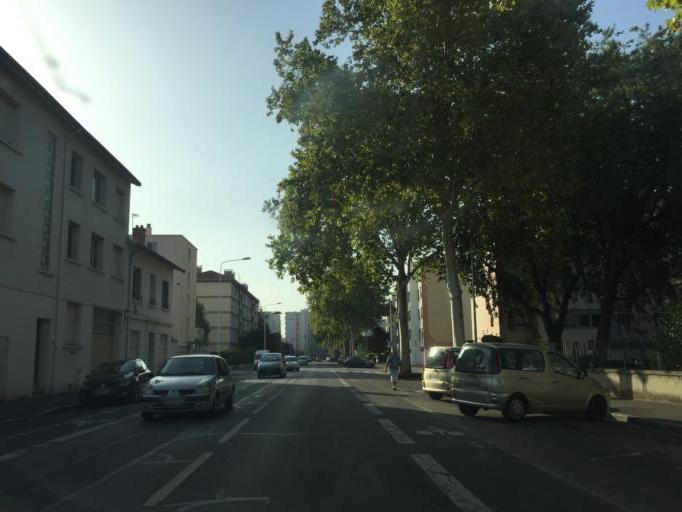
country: FR
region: Rhone-Alpes
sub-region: Departement du Rhone
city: Venissieux
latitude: 45.7277
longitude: 4.8836
